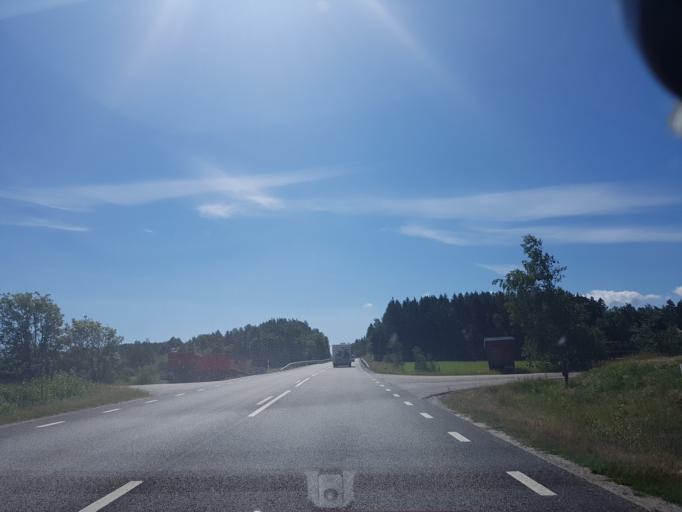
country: SE
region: Vaestra Goetaland
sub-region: Orust
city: Henan
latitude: 58.1395
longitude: 11.6462
